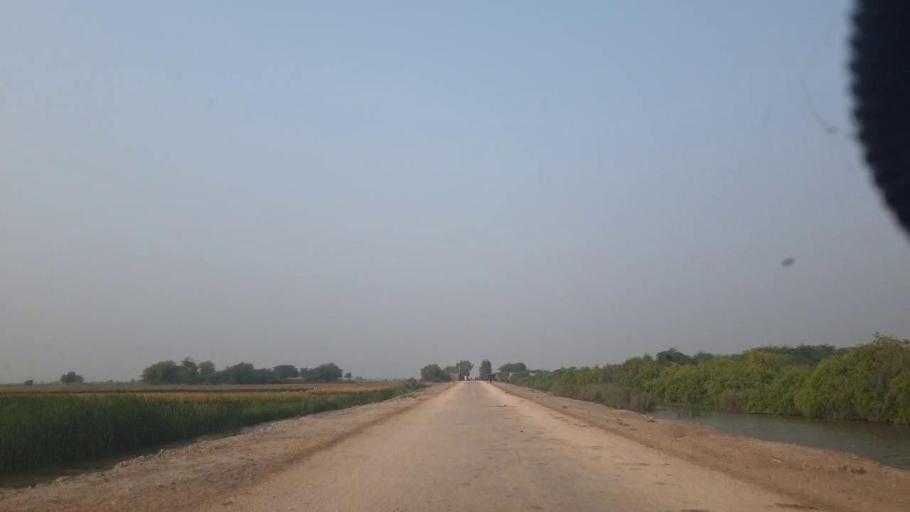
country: PK
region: Sindh
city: Bulri
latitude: 24.8351
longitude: 68.4031
